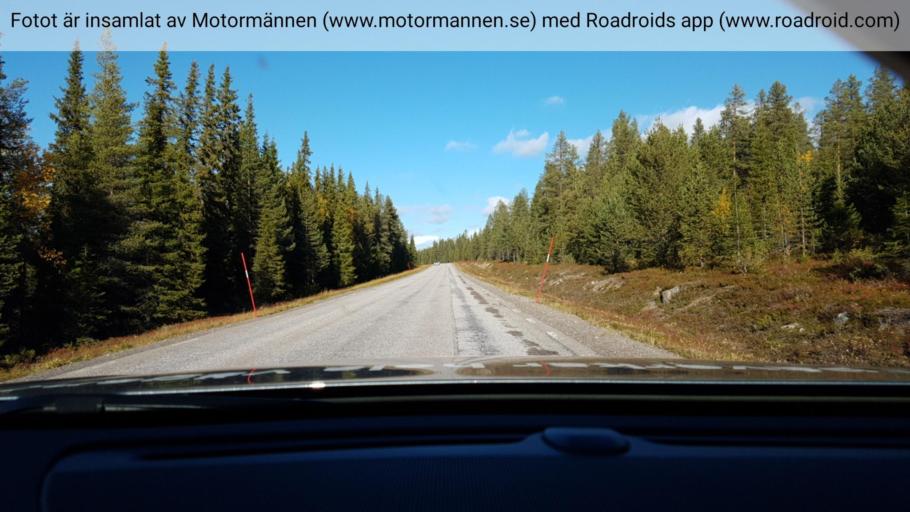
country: SE
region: Norrbotten
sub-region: Arjeplogs Kommun
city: Arjeplog
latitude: 65.8033
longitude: 18.4661
